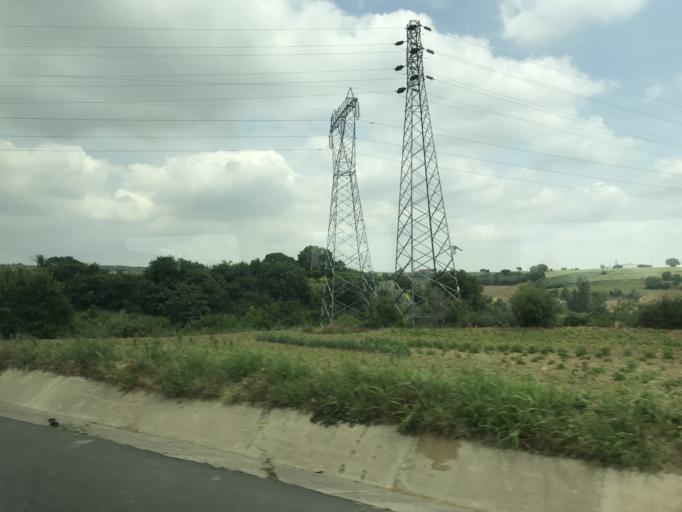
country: TR
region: Tekirdag
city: Tekirdag
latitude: 41.0030
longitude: 27.5437
